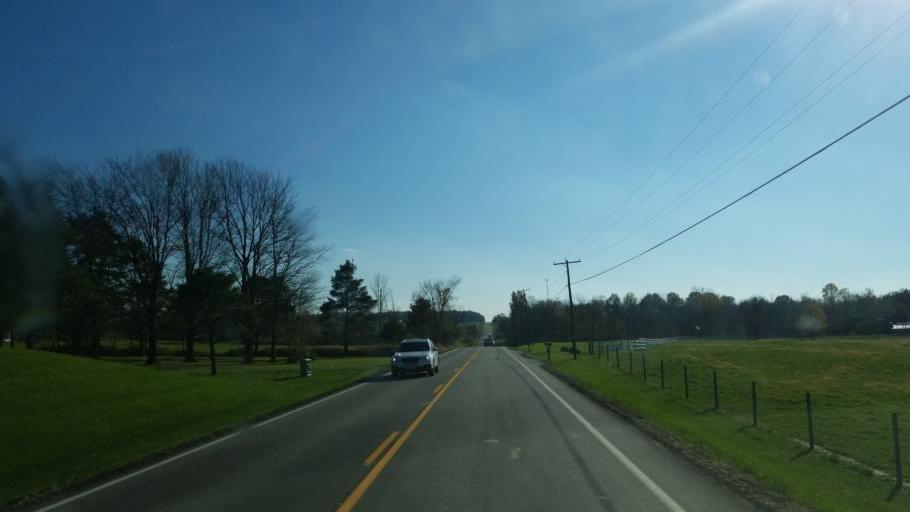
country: US
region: Ohio
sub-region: Wayne County
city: West Salem
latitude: 40.9712
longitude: -82.2151
